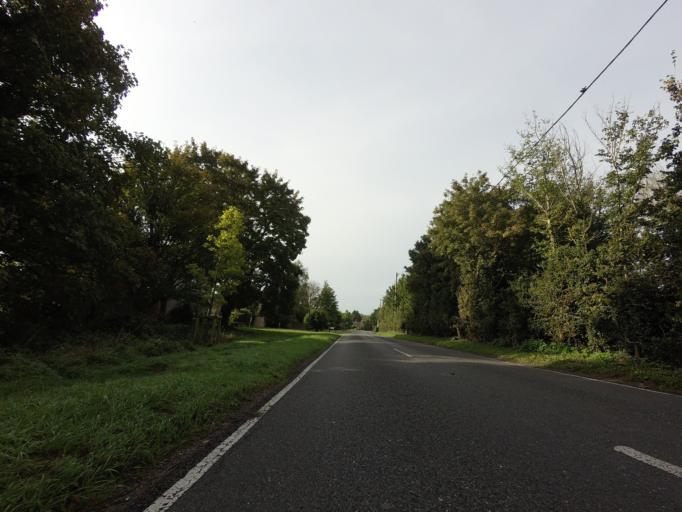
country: GB
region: England
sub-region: Cambridgeshire
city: Harston
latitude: 52.0957
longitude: 0.0795
